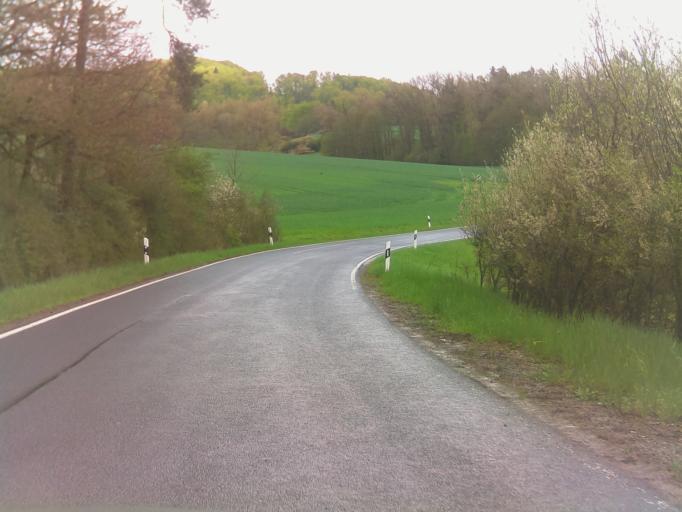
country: DE
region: Thuringia
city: Kloster Vessra
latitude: 50.5021
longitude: 10.6561
